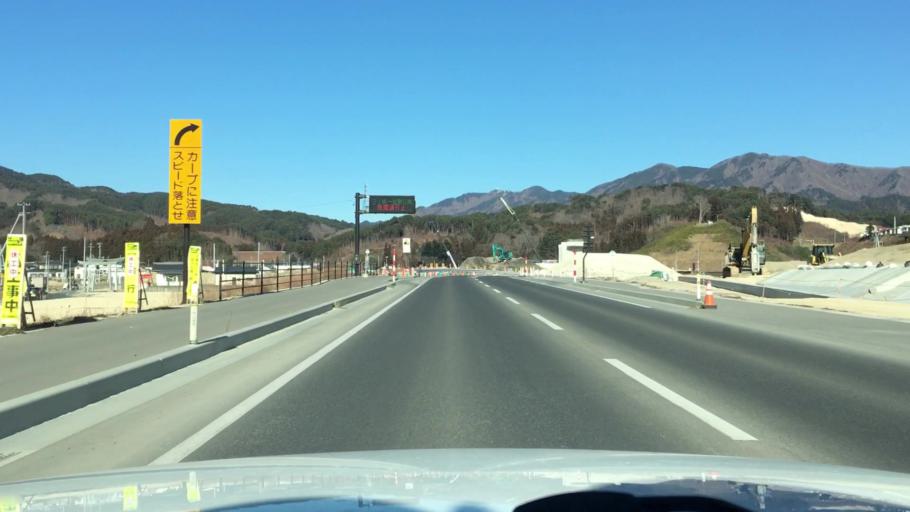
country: JP
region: Iwate
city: Yamada
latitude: 39.4710
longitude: 141.9531
